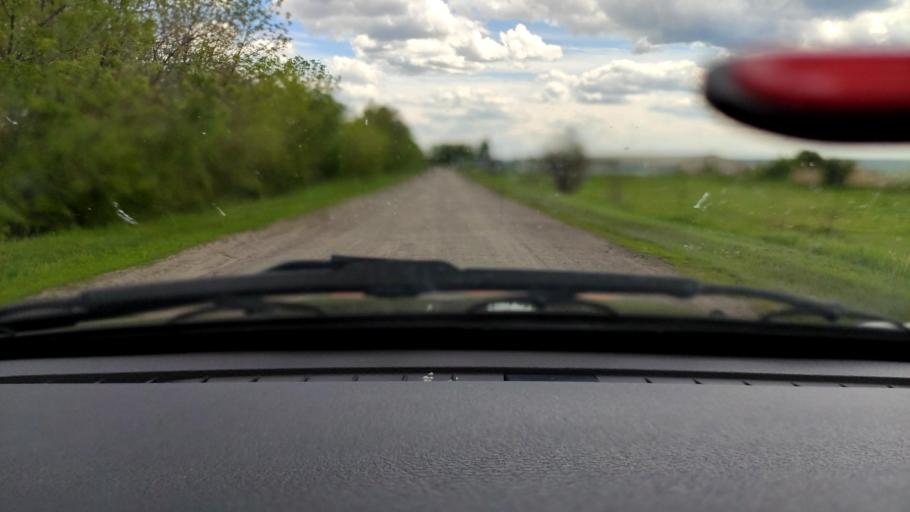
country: RU
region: Voronezj
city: Uryv-Pokrovka
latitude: 51.1158
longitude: 39.1442
